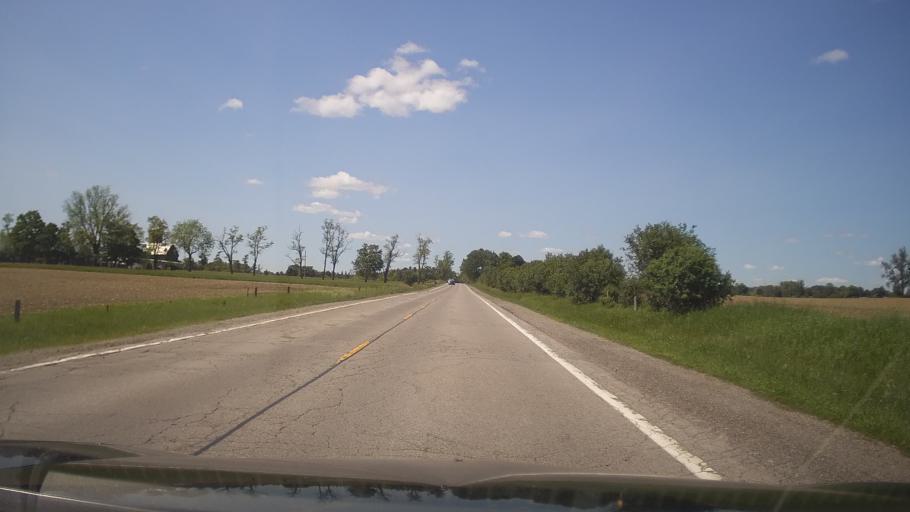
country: CA
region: Ontario
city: Oshawa
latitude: 43.9870
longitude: -78.8595
